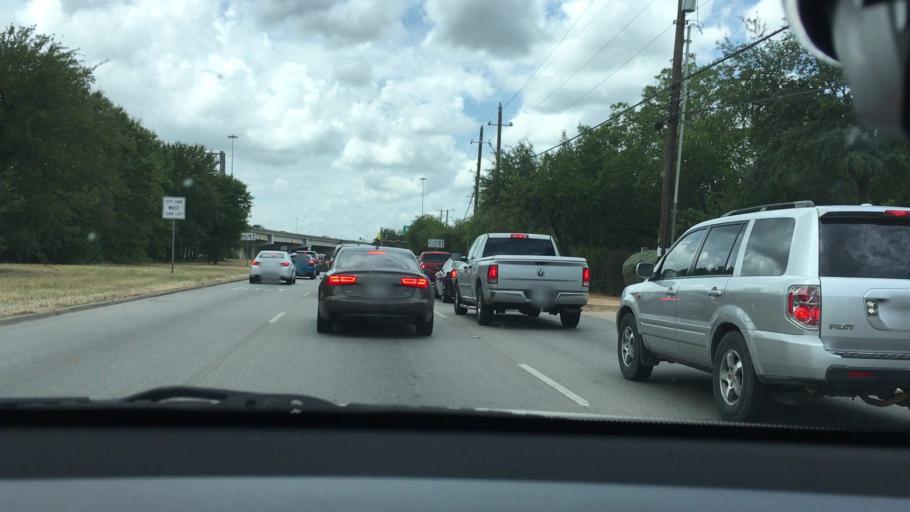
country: US
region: Texas
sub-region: Travis County
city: Rollingwood
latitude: 30.2337
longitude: -97.8161
